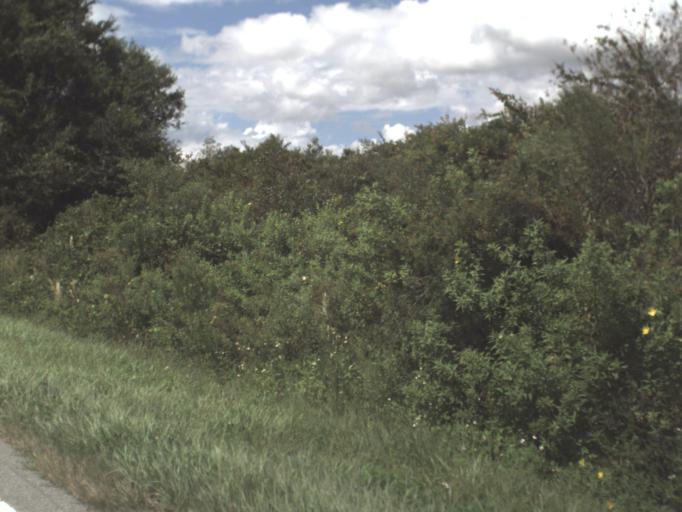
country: US
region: Florida
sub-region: Hillsborough County
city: Balm
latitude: 27.6417
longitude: -82.0600
